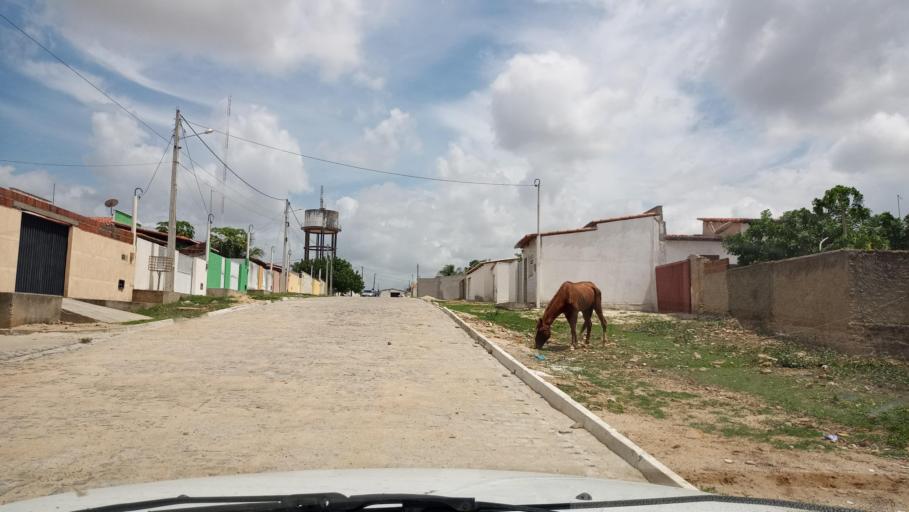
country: BR
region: Rio Grande do Norte
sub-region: Tangara
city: Tangara
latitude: -6.1085
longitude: -35.7142
